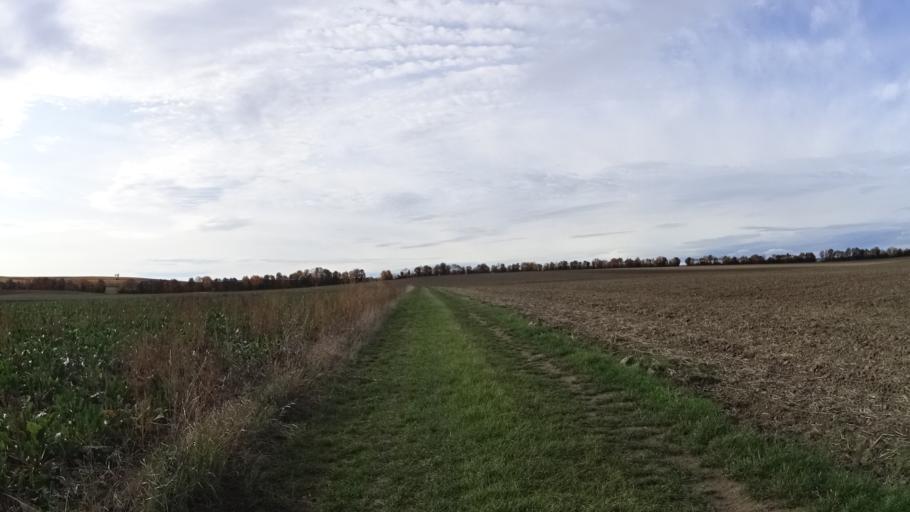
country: DE
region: Rheinland-Pfalz
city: Eckelsheim
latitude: 49.8027
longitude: 8.0035
